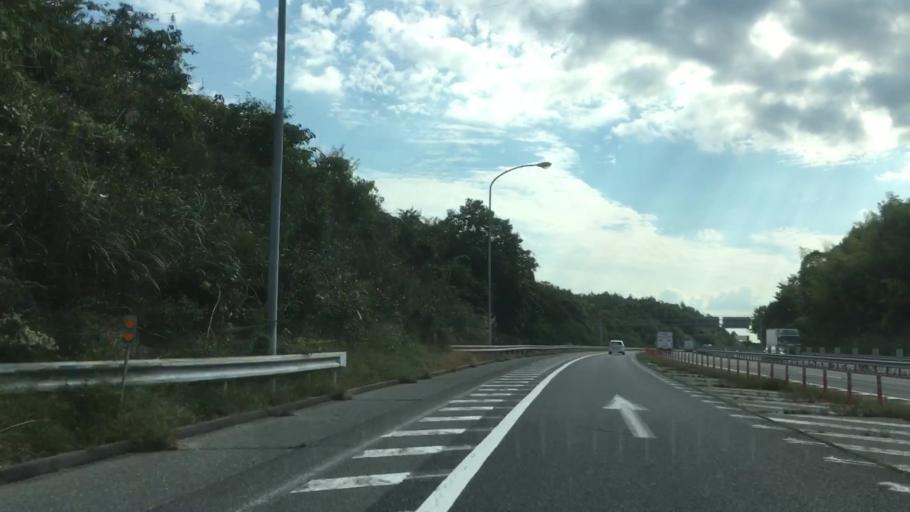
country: JP
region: Hiroshima
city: Miyajima
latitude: 34.3298
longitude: 132.2939
